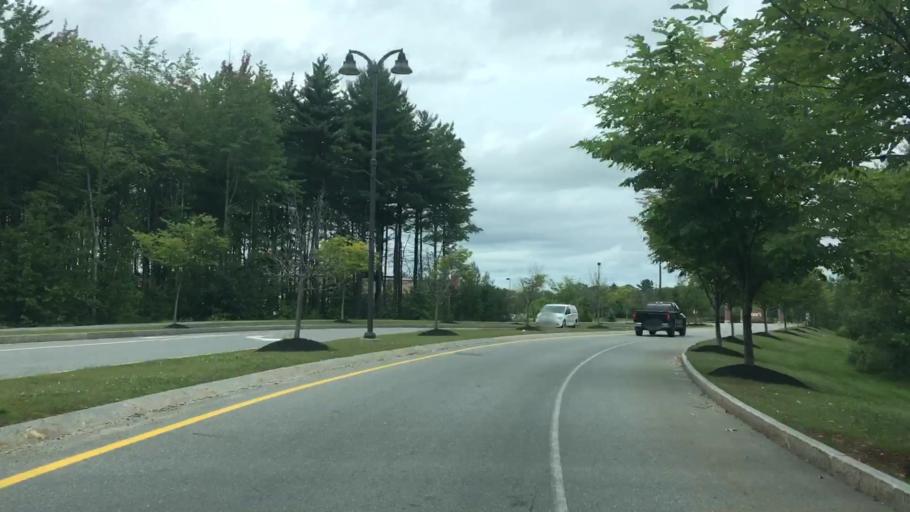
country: US
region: Maine
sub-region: Cumberland County
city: South Portland Gardens
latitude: 43.6214
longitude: -70.3394
